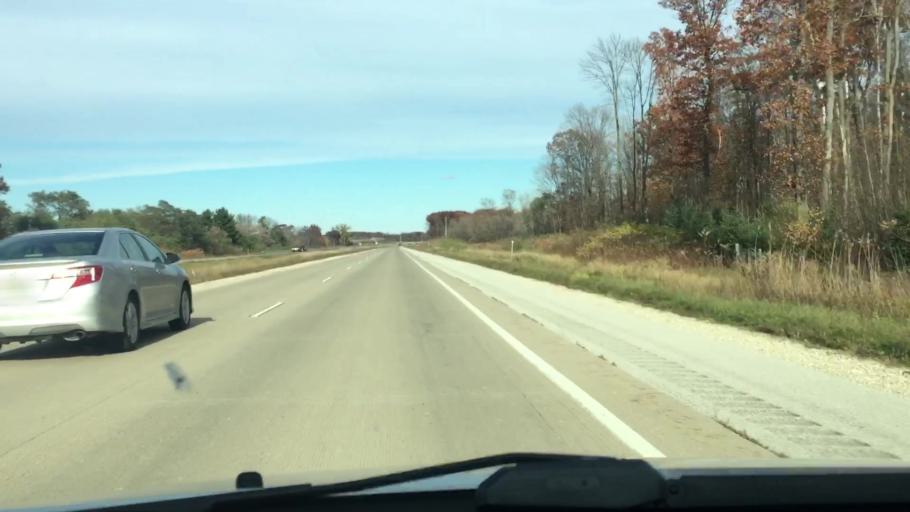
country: US
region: Wisconsin
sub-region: Kewaunee County
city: Luxemburg
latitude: 44.6973
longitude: -87.7123
